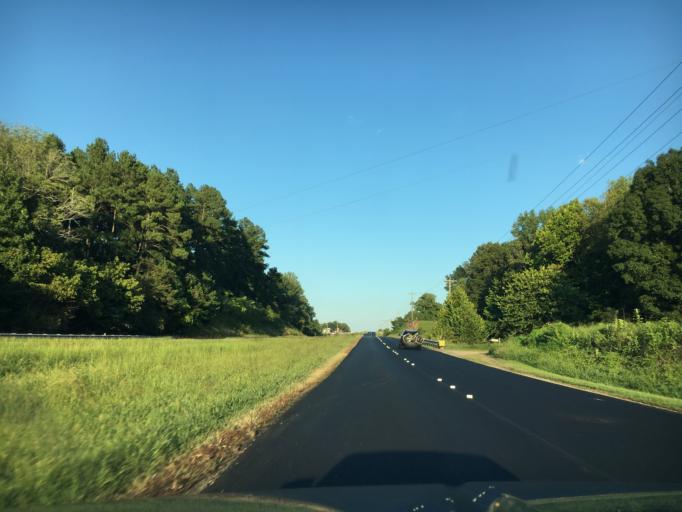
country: US
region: Virginia
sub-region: City of Danville
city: Danville
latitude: 36.5806
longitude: -79.2517
